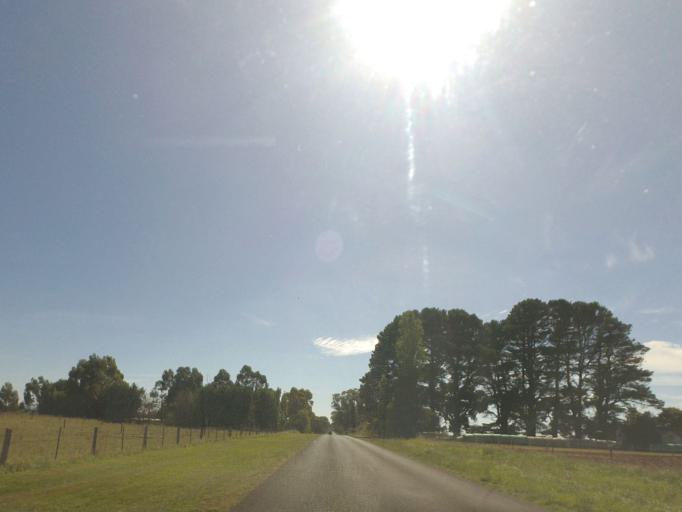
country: AU
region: Victoria
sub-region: Moorabool
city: Bacchus Marsh
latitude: -37.3737
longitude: 144.3900
